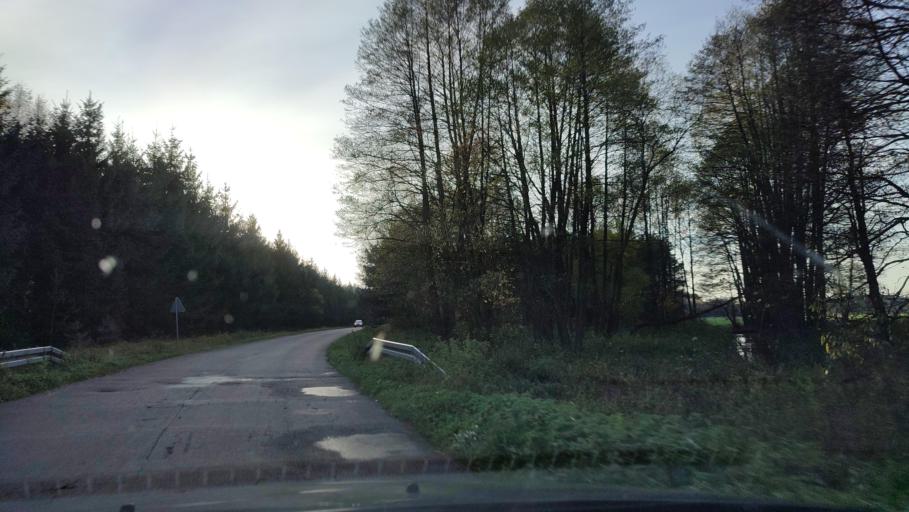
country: PL
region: Masovian Voivodeship
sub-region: Powiat mlawski
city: Dzierzgowo
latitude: 53.3287
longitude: 20.6982
